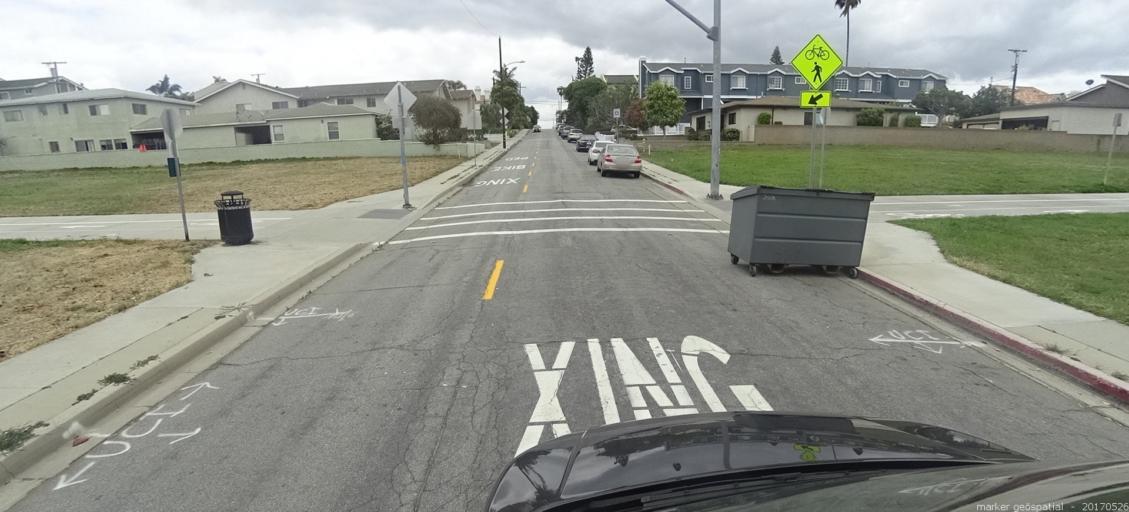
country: US
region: California
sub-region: Los Angeles County
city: Lawndale
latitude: 33.8757
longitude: -118.3660
